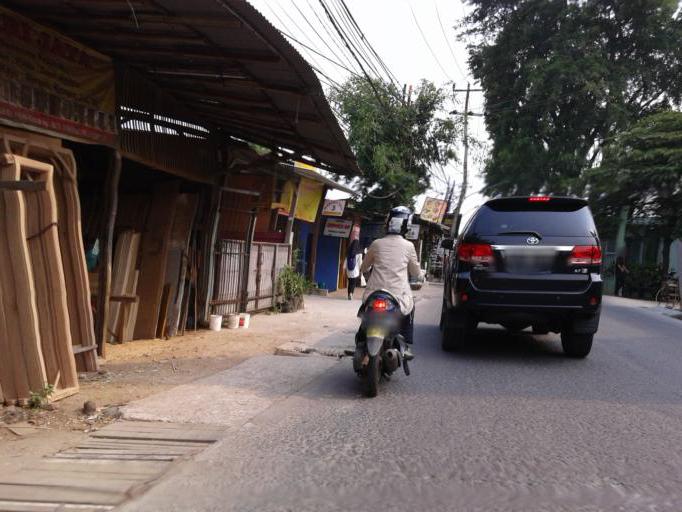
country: ID
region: West Java
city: Pamulang
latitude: -6.3547
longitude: 106.7755
